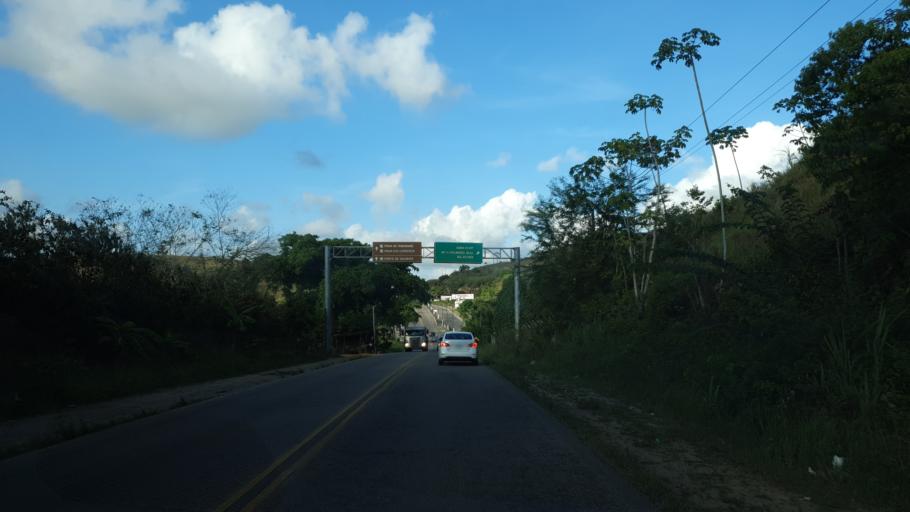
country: BR
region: Pernambuco
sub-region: Barreiros
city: Barreiros
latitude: -8.7930
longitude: -35.1870
